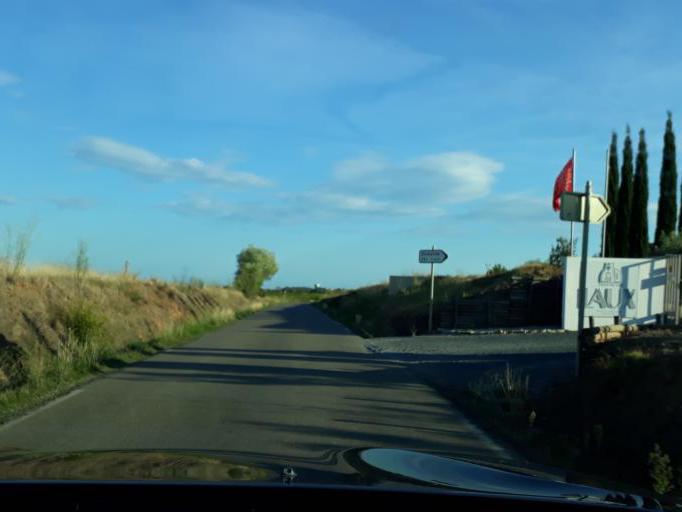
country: FR
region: Languedoc-Roussillon
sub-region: Departement de l'Herault
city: Pomerols
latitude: 43.3821
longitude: 3.5077
